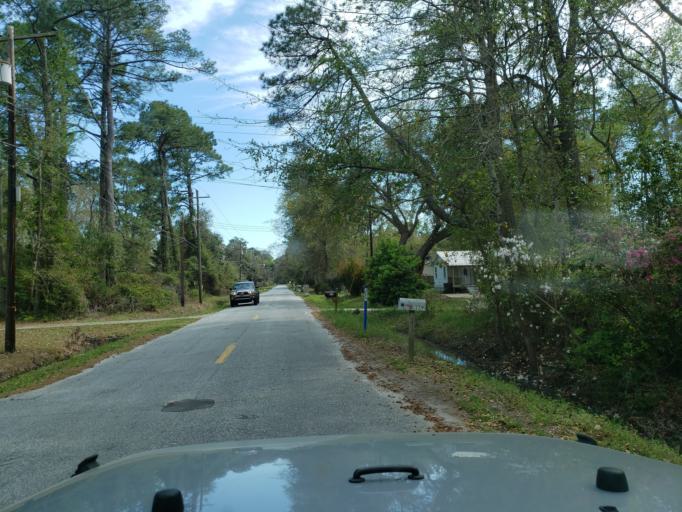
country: US
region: Georgia
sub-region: Chatham County
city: Montgomery
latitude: 31.9512
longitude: -81.1138
